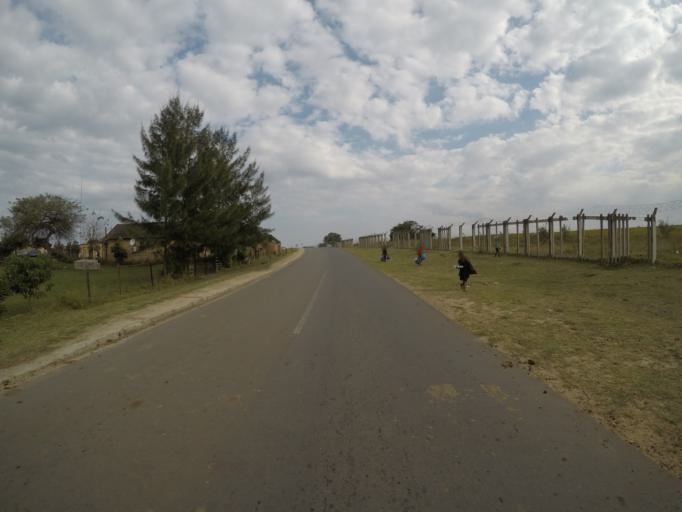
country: ZA
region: KwaZulu-Natal
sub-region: uThungulu District Municipality
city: Richards Bay
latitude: -28.7422
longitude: 32.0928
